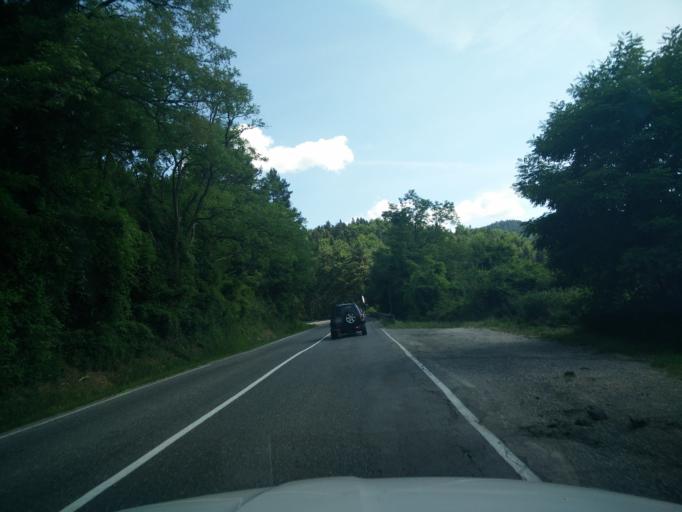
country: SK
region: Nitriansky
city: Prievidza
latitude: 48.8953
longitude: 18.6999
